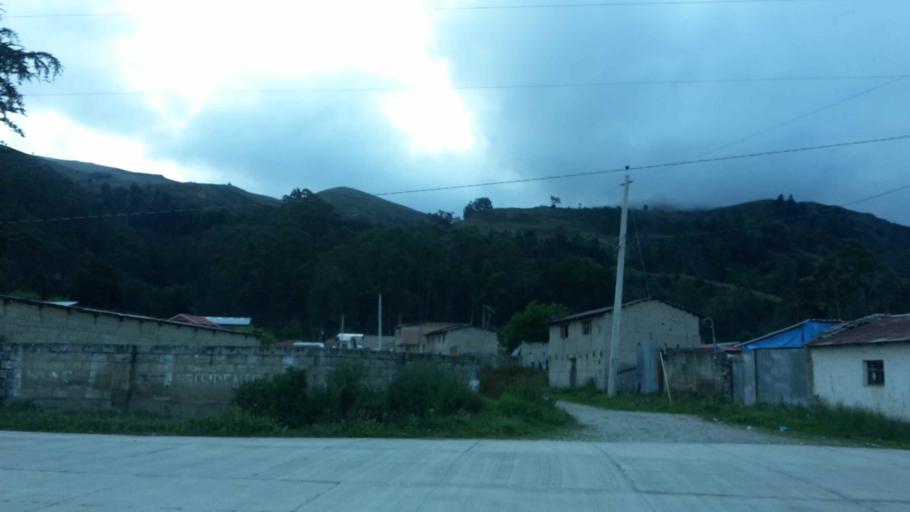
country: BO
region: Cochabamba
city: Colomi
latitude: -17.2742
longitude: -65.9258
